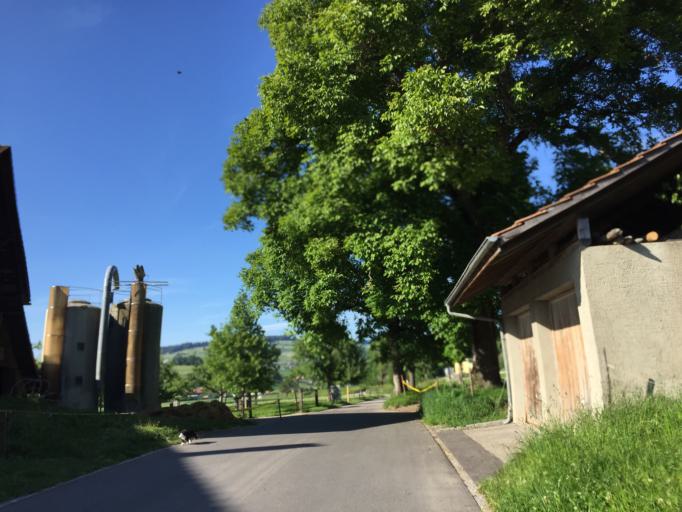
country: CH
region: Bern
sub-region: Bern-Mittelland District
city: Konolfingen
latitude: 46.8786
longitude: 7.6363
